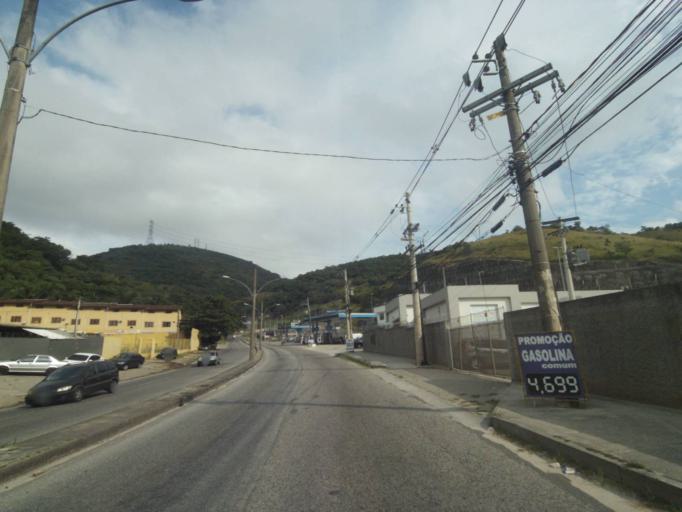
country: BR
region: Rio de Janeiro
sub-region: Nilopolis
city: Nilopolis
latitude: -22.8962
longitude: -43.3982
